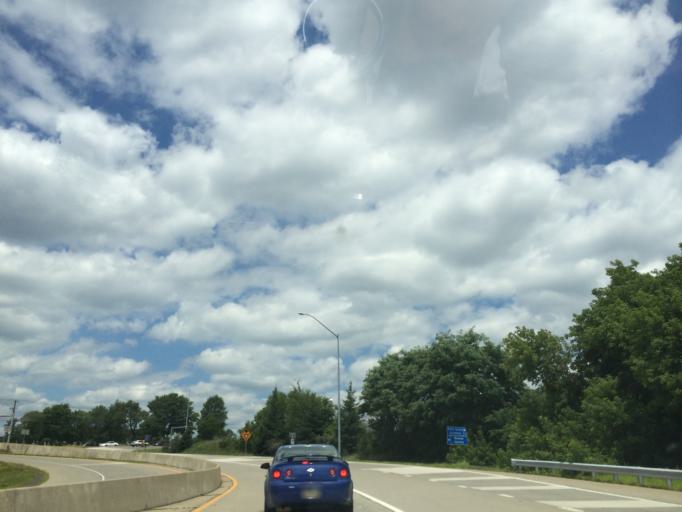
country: US
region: Pennsylvania
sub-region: Lackawanna County
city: Dunmore
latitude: 41.4312
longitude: -75.6207
